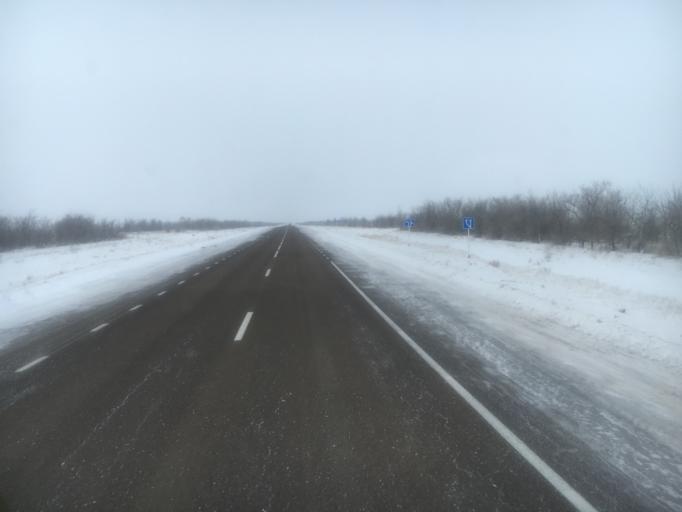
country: KZ
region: Aqtoebe
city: Martuk
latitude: 50.1557
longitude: 55.5461
